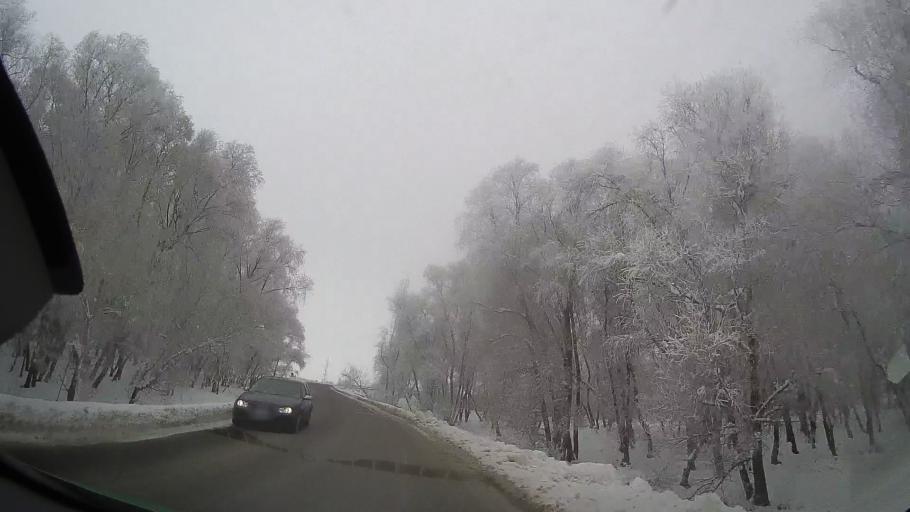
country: RO
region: Neamt
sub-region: Comuna Horia
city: Cotu Vames
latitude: 46.8808
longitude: 26.9730
